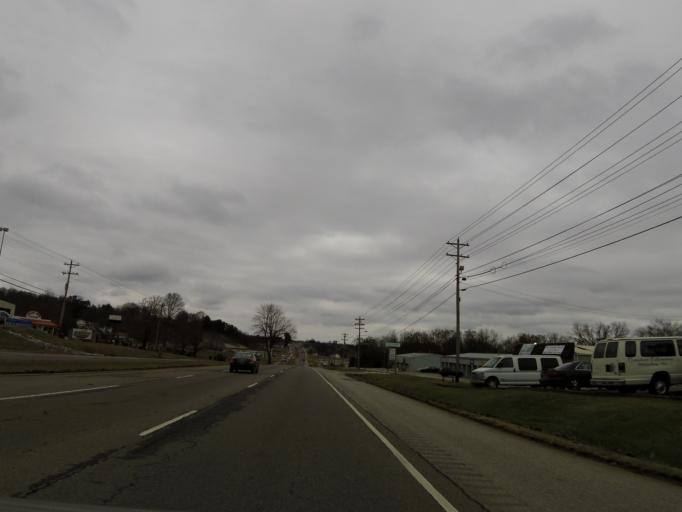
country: US
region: Tennessee
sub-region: Hamblen County
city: Morristown
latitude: 36.1826
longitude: -83.3796
